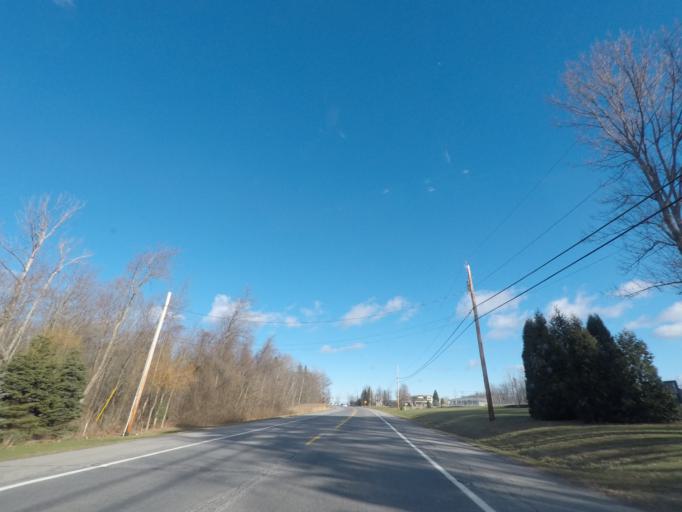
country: US
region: New York
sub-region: Saratoga County
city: Mechanicville
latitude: 42.8508
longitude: -73.7288
